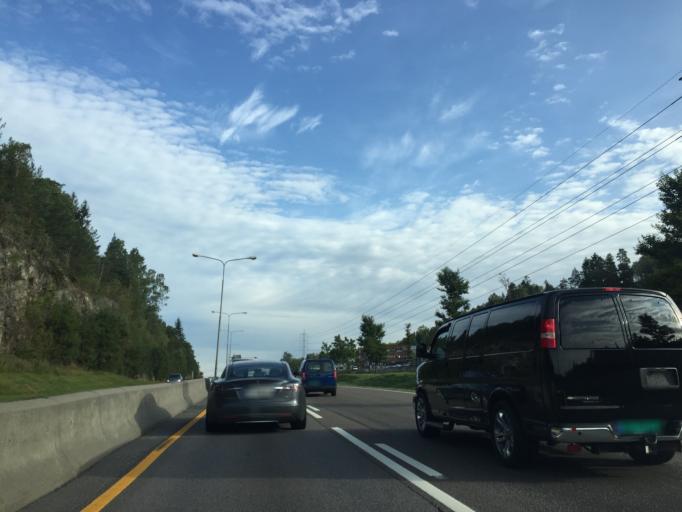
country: NO
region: Akershus
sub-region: Oppegard
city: Kolbotn
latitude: 59.8661
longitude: 10.8304
